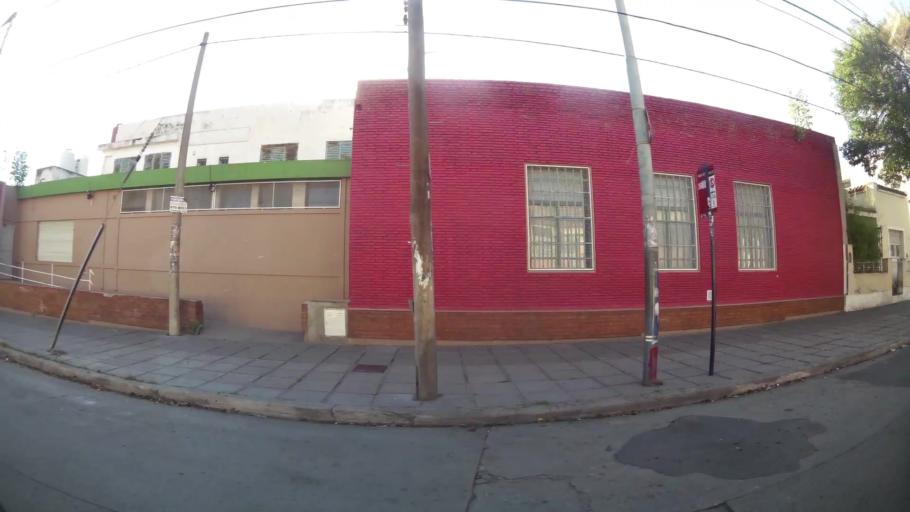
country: AR
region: Cordoba
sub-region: Departamento de Capital
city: Cordoba
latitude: -31.3802
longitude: -64.1839
